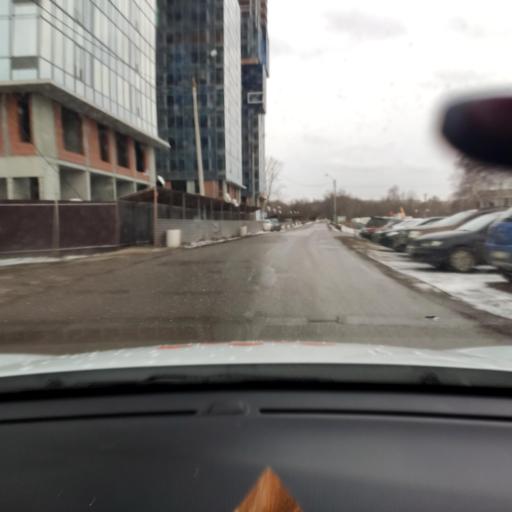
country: RU
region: Tatarstan
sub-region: Gorod Kazan'
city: Kazan
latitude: 55.8077
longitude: 49.0917
